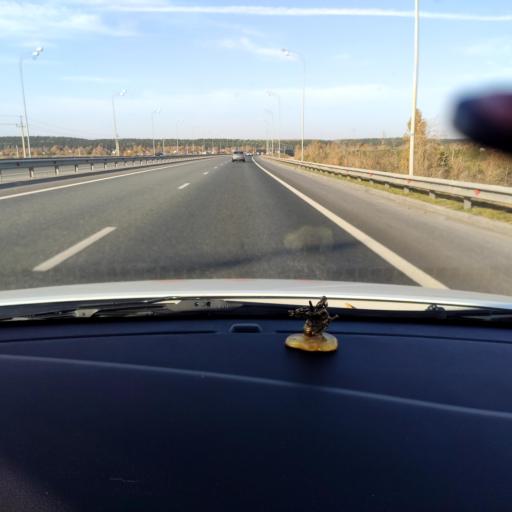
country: RU
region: Tatarstan
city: Osinovo
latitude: 55.8118
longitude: 48.8419
